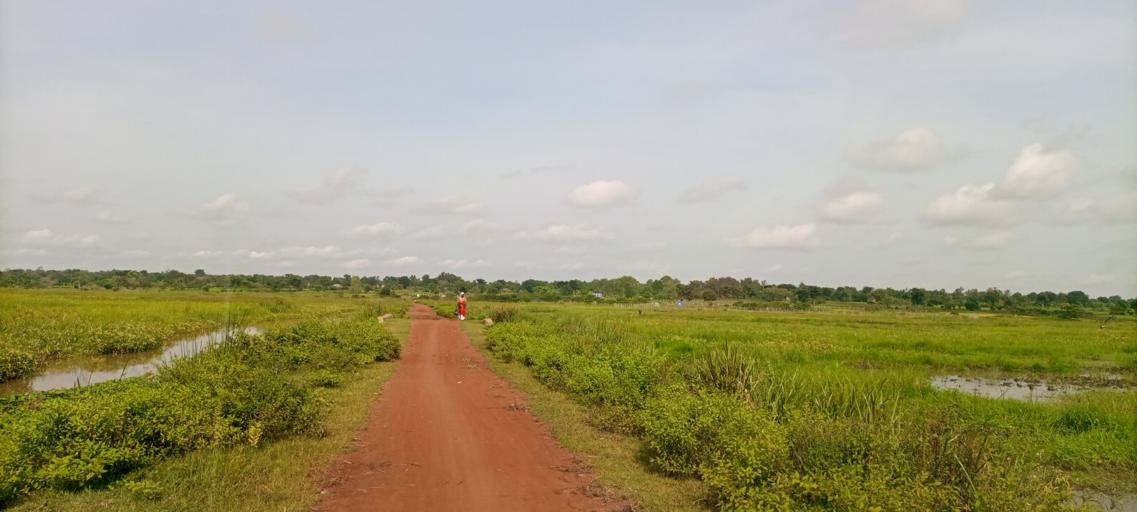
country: UG
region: Eastern Region
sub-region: Kibuku District
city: Kibuku
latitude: 1.0991
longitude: 33.7731
